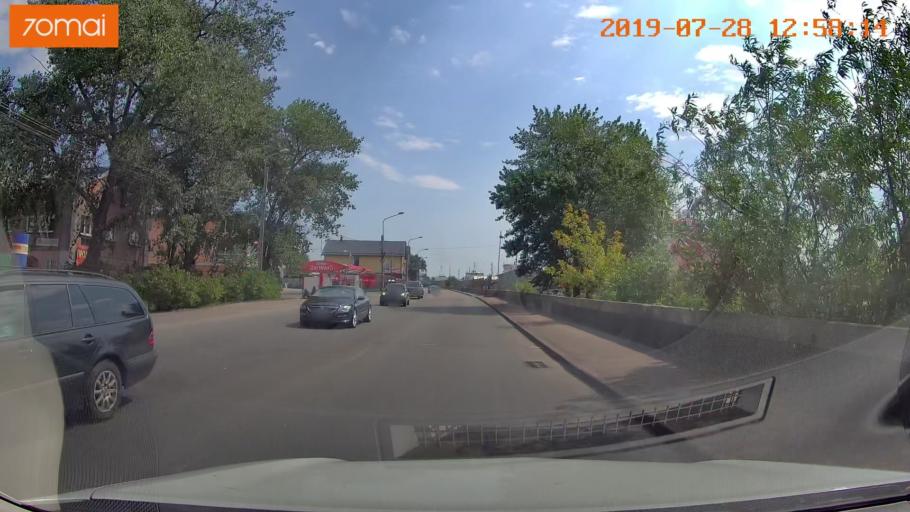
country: RU
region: Kaliningrad
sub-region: Gorod Kaliningrad
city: Kaliningrad
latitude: 54.7056
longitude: 20.4737
